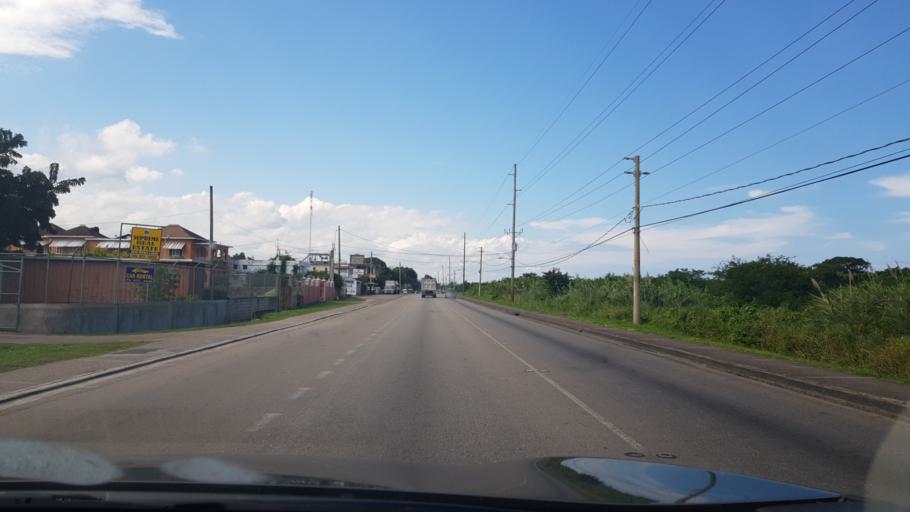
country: JM
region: Saint Ann
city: Runaway Bay
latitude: 18.4669
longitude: -77.3082
